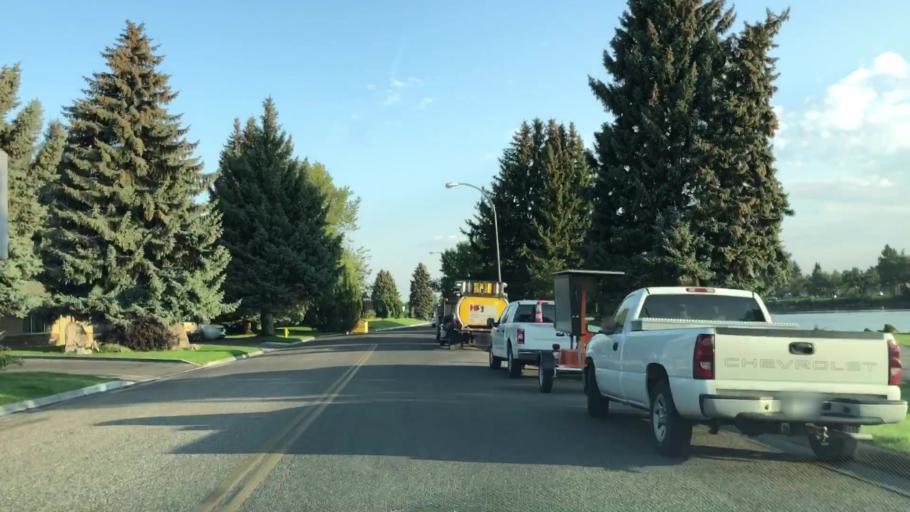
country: US
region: Idaho
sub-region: Bonneville County
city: Idaho Falls
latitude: 43.4982
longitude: -112.0442
